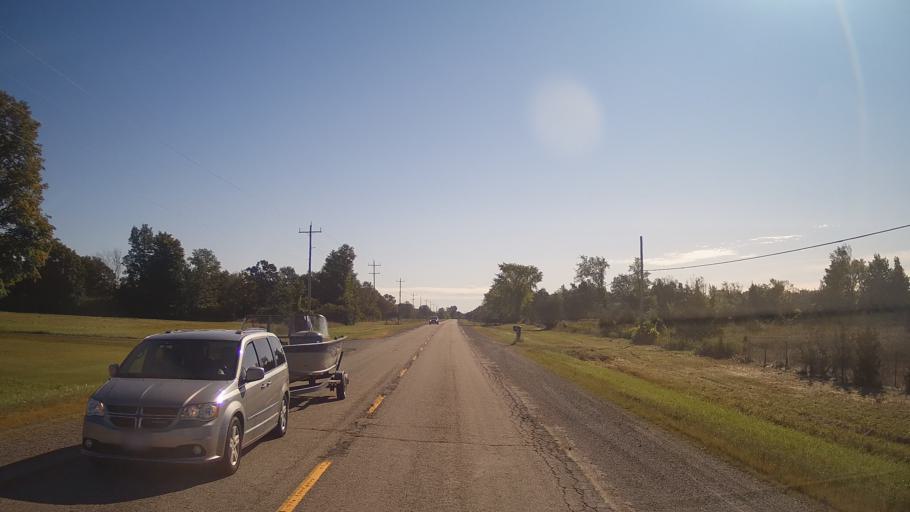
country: CA
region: Ontario
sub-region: Lanark County
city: Smiths Falls
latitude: 44.6267
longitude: -76.0264
